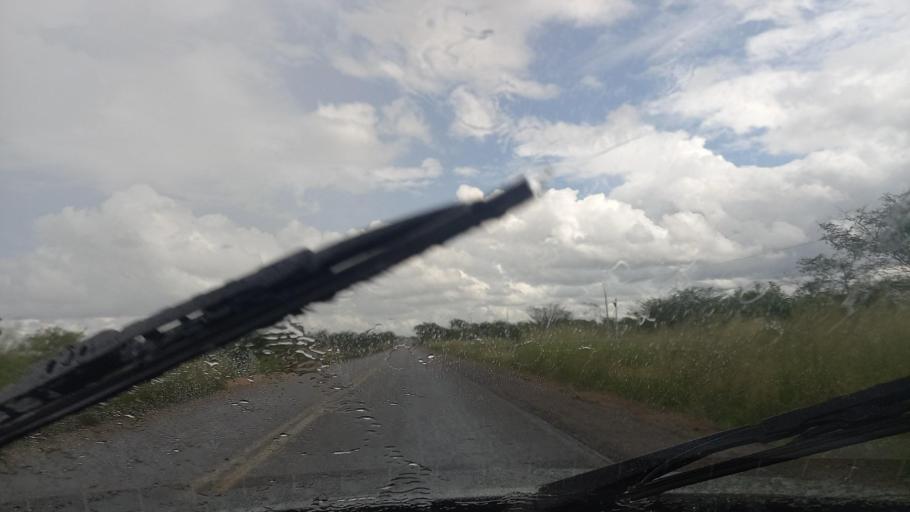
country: BR
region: Pernambuco
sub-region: Cachoeirinha
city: Cachoeirinha
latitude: -8.5555
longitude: -36.2744
